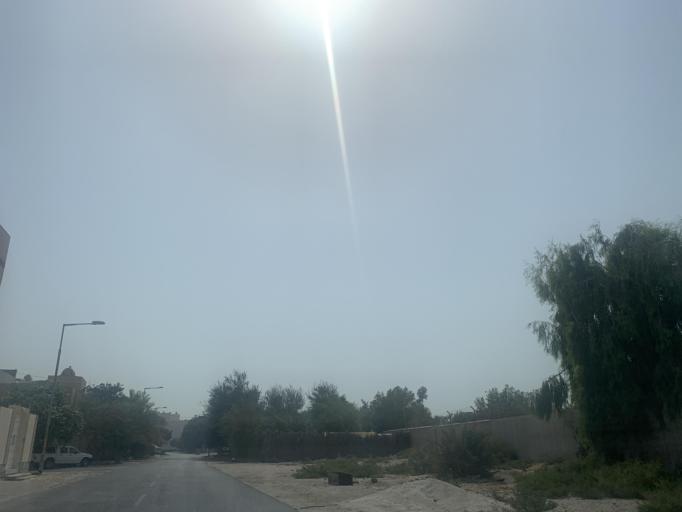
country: BH
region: Manama
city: Jidd Hafs
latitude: 26.2092
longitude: 50.4655
